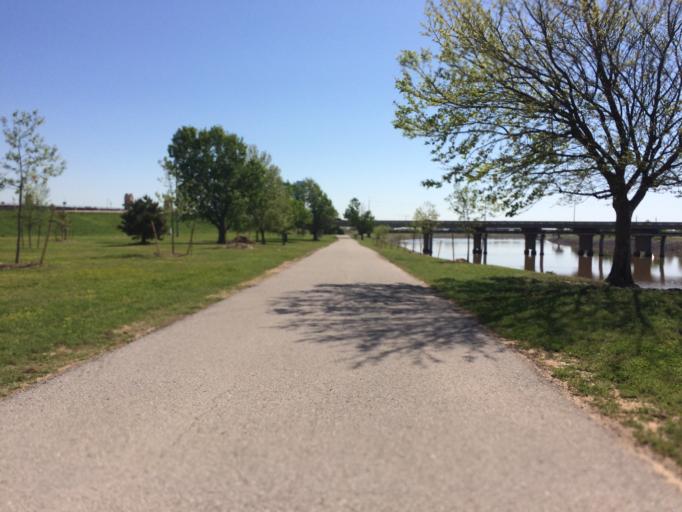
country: US
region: Oklahoma
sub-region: Oklahoma County
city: Oklahoma City
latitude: 35.4605
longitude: -97.5503
